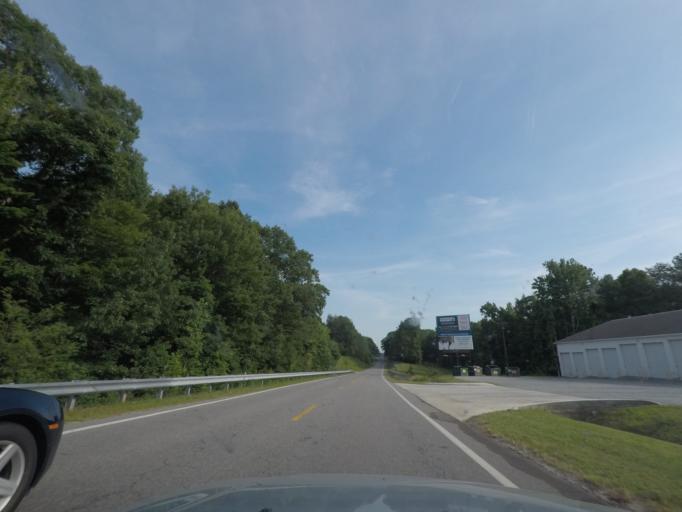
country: US
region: Virginia
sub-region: Mecklenburg County
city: Clarksville
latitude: 36.5885
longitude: -78.5482
